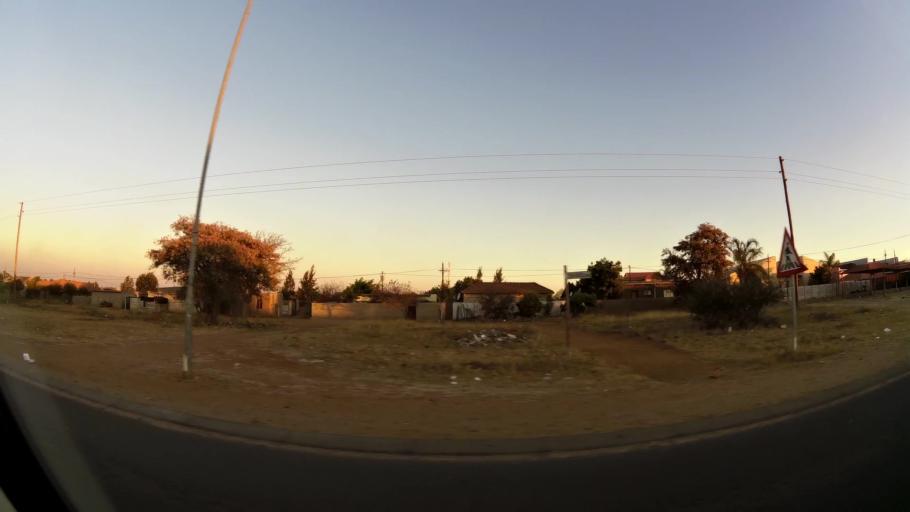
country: ZA
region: Limpopo
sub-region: Capricorn District Municipality
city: Polokwane
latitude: -23.8534
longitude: 29.3666
